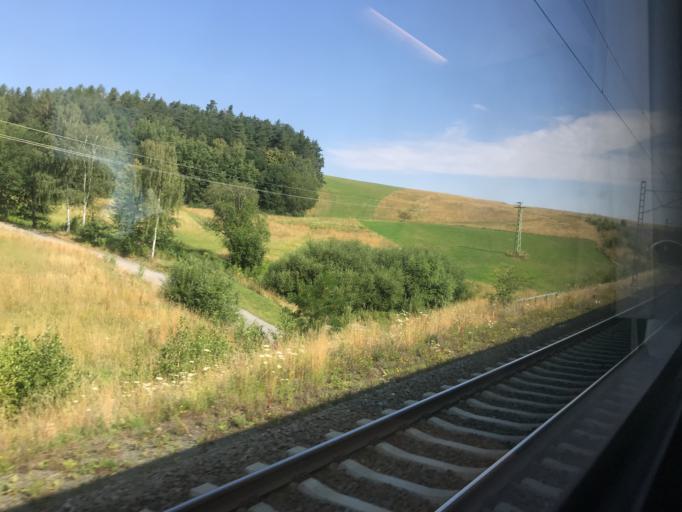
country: CZ
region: Central Bohemia
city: Votice
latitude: 49.6480
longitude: 14.6256
